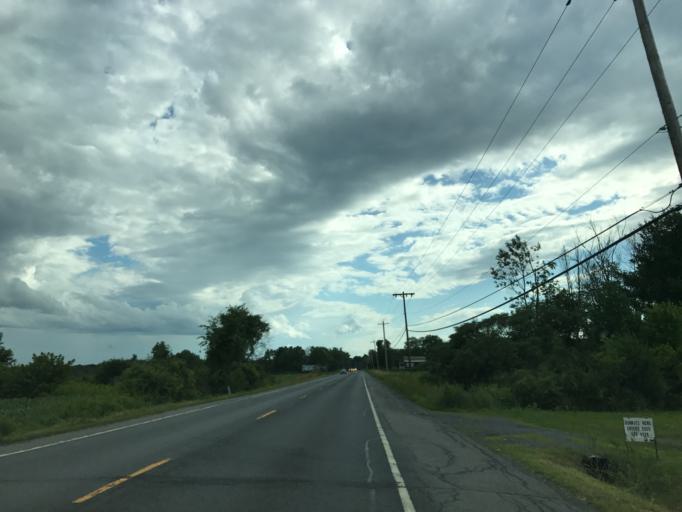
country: US
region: New York
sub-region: Washington County
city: Hudson Falls
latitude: 43.3369
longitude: -73.5554
